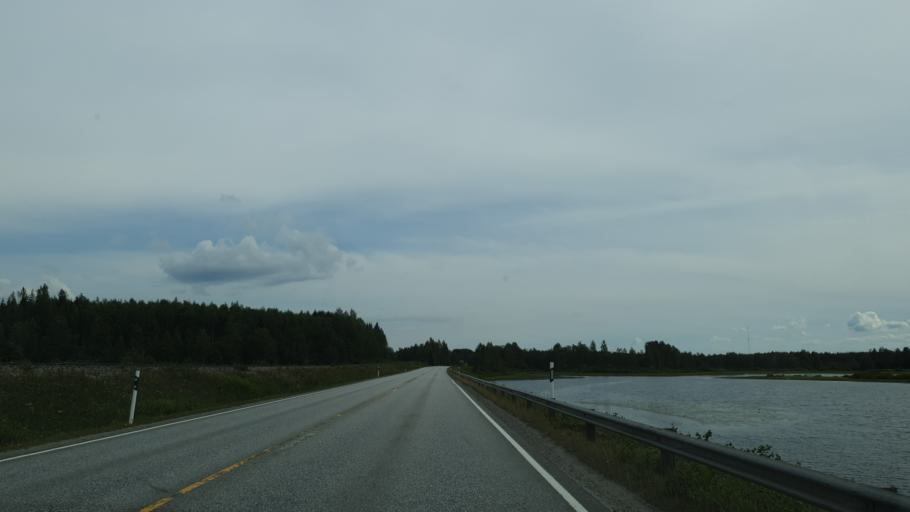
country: FI
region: North Karelia
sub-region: Pielisen Karjala
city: Valtimo
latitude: 63.7018
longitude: 28.7695
